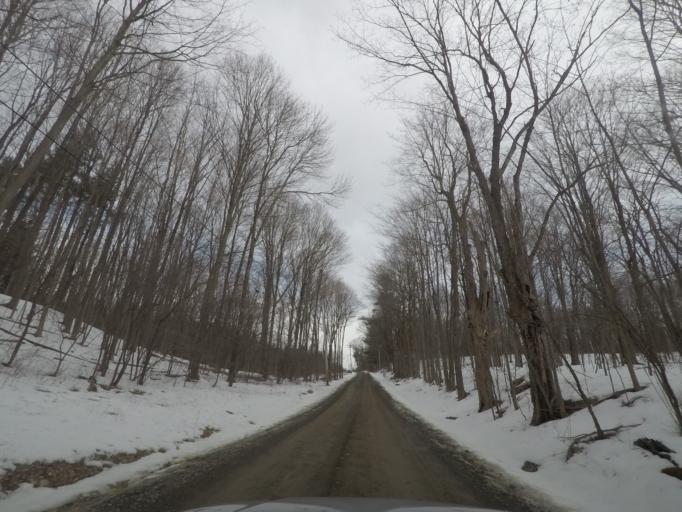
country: US
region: New York
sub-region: Saratoga County
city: Waterford
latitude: 42.7836
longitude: -73.6111
